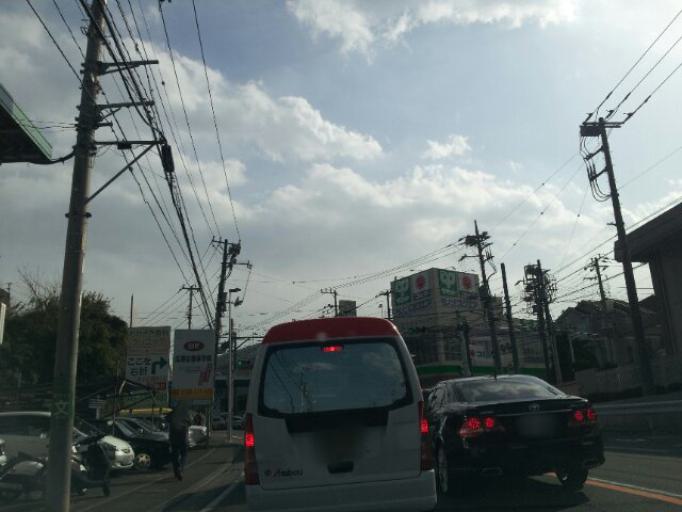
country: JP
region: Kanagawa
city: Yokohama
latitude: 35.4396
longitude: 139.5751
